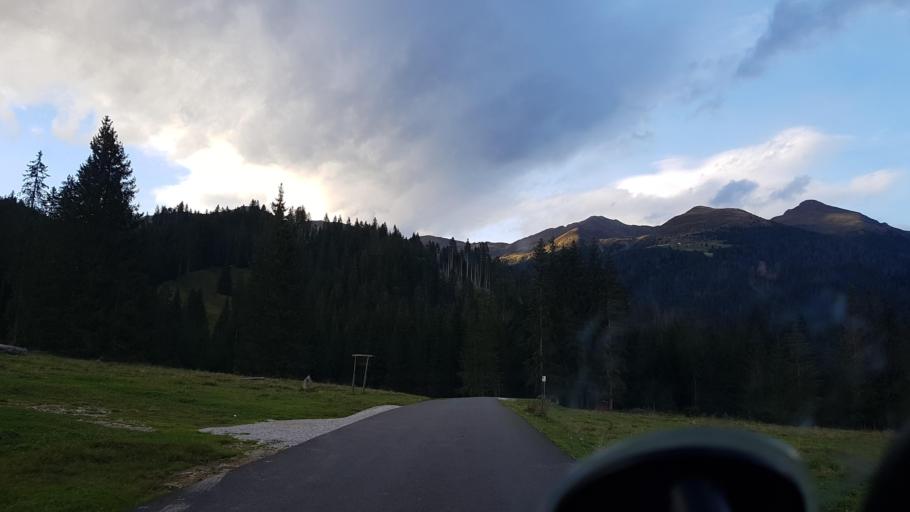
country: IT
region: Veneto
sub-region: Provincia di Belluno
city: San Pietro di Cadore
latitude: 46.6143
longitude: 12.6242
